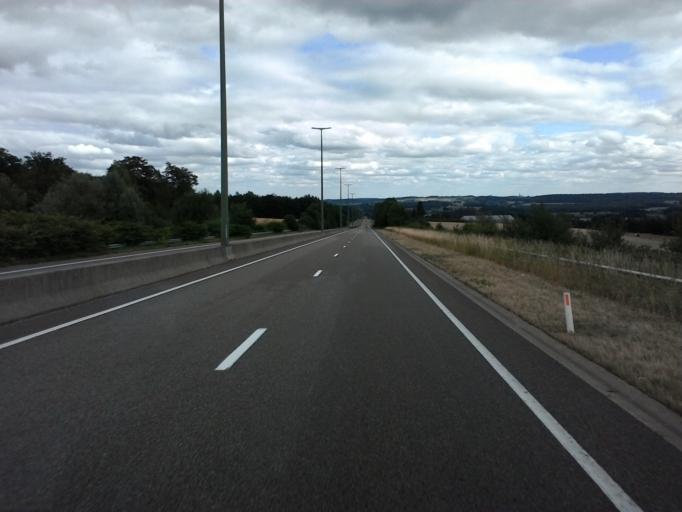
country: BE
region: Wallonia
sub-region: Province du Luxembourg
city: Attert
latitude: 49.7740
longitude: 5.7595
